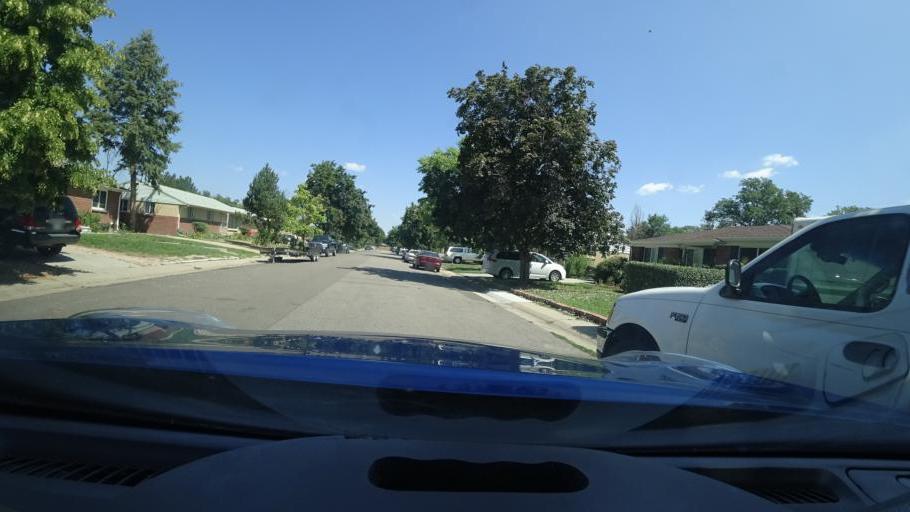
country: US
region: Colorado
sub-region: Adams County
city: Aurora
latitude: 39.7235
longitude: -104.8716
